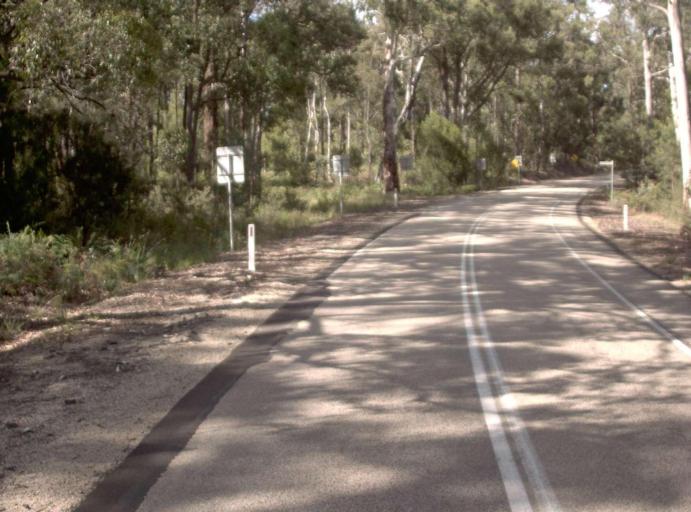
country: AU
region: Victoria
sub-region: East Gippsland
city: Lakes Entrance
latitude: -37.5250
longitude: 148.1607
